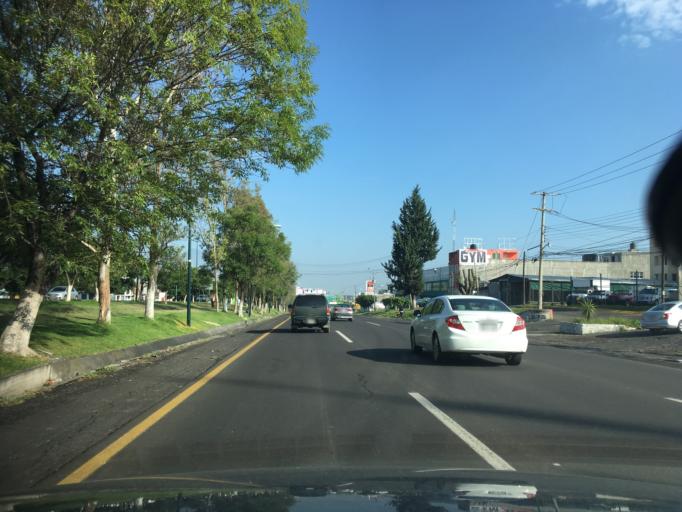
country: MX
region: Michoacan
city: Morelia
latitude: 19.7029
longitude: -101.1579
